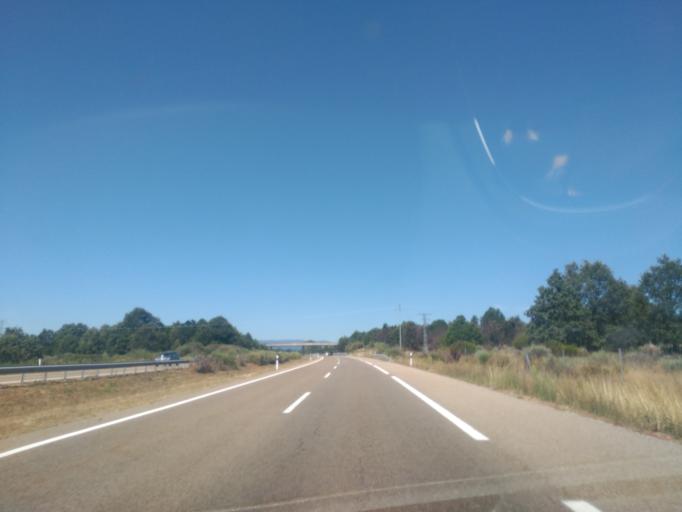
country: ES
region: Castille and Leon
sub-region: Provincia de Zamora
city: Asturianos
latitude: 42.0420
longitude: -6.4667
